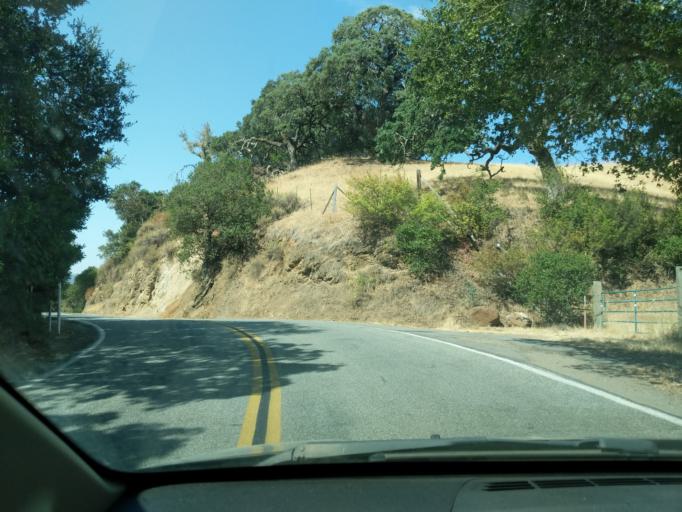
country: US
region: California
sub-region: Santa Clara County
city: Gilroy
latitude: 37.0562
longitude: -121.5229
